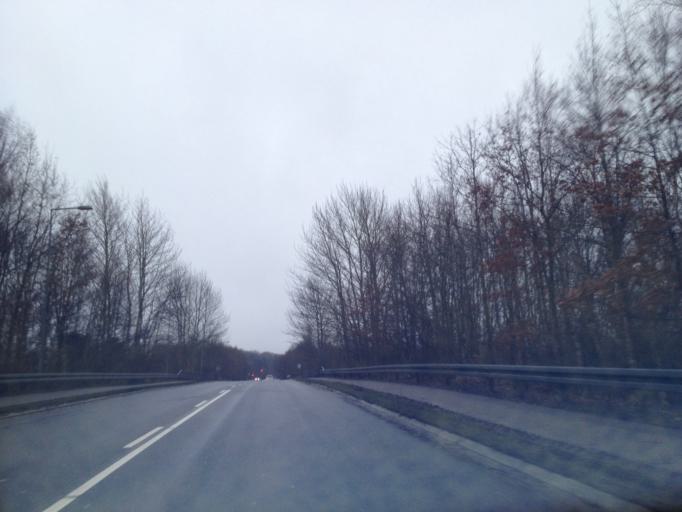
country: DK
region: Capital Region
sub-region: Hoje-Taastrup Kommune
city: Flong
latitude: 55.6512
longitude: 12.1775
